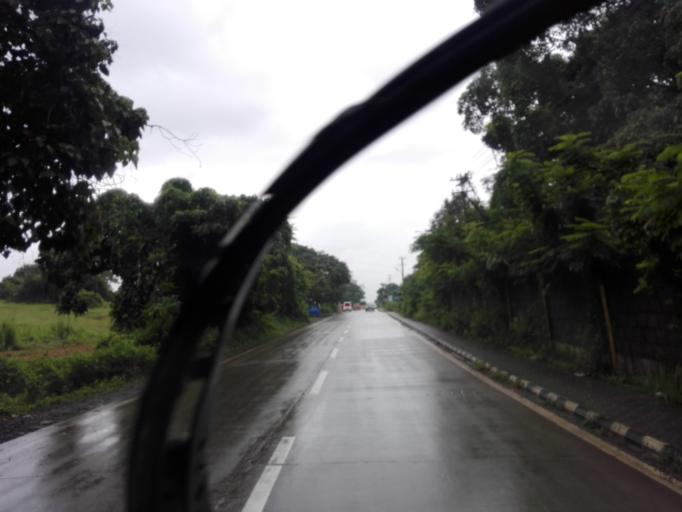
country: IN
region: Kerala
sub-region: Ernakulam
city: Aluva
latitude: 10.0493
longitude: 76.3422
